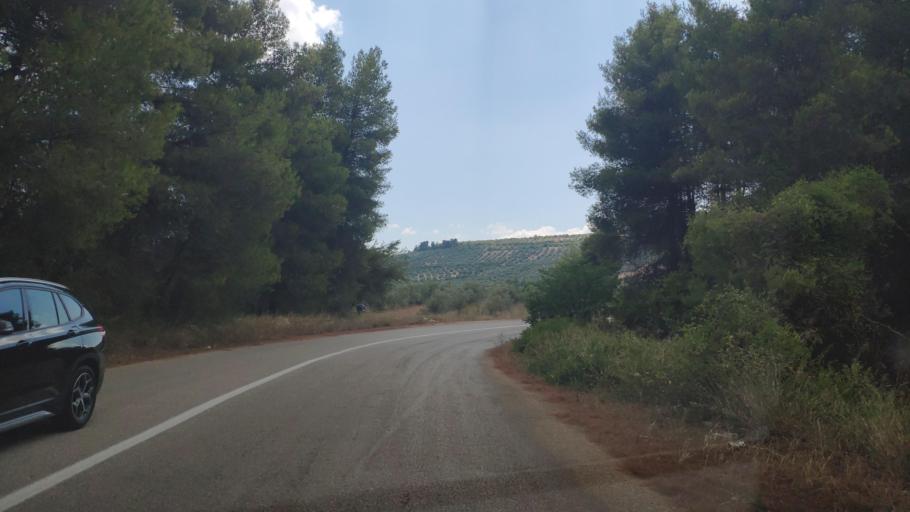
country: GR
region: Central Greece
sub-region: Nomos Fthiotidos
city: Malesina
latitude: 38.6185
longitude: 23.1819
